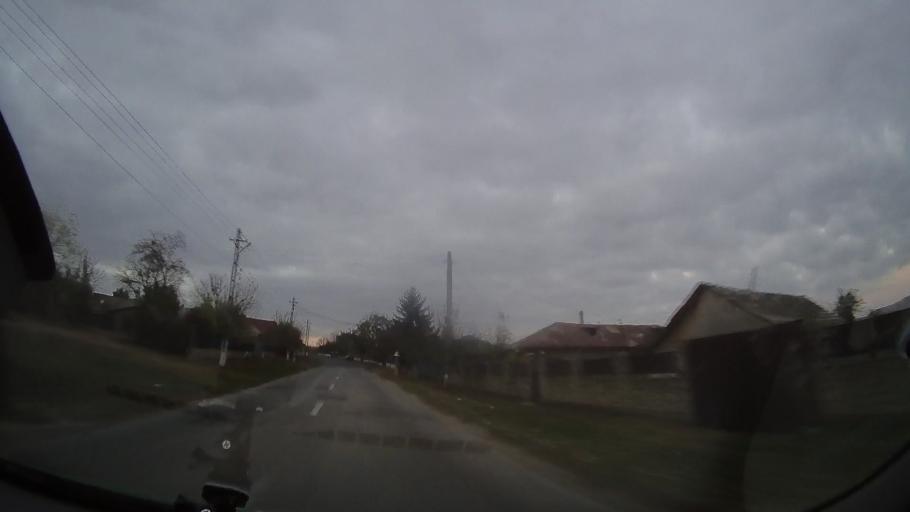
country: RO
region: Tulcea
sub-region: Comuna Mihai Bravu
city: Turda
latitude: 44.9703
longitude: 28.6279
